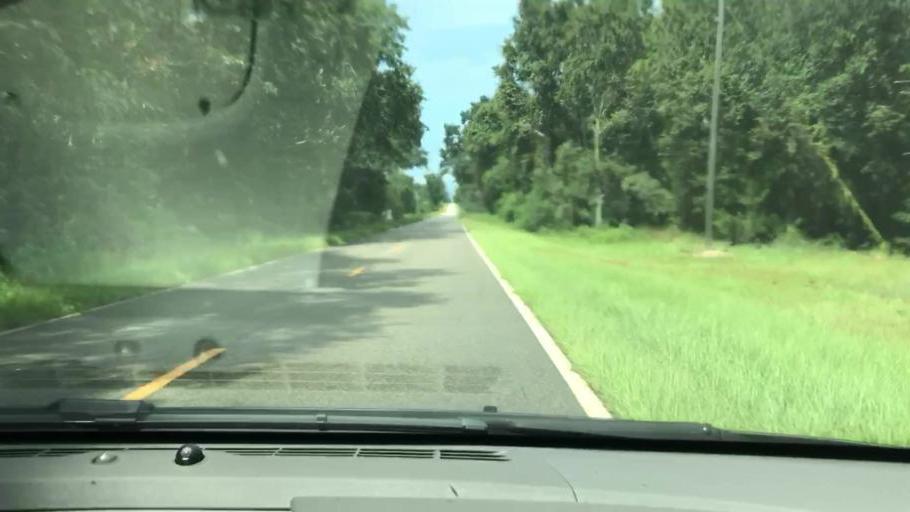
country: US
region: Georgia
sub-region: Seminole County
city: Donalsonville
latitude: 31.1210
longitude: -84.9956
